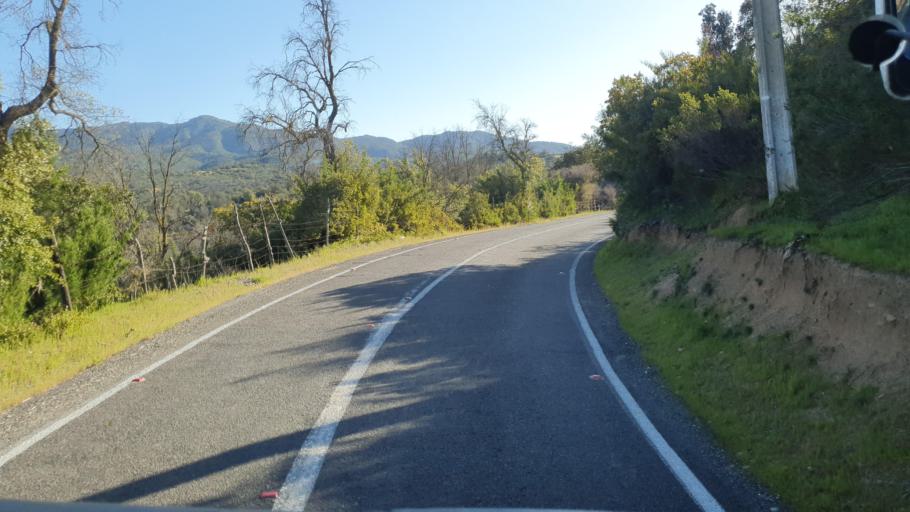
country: CL
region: Valparaiso
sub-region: Provincia de Marga Marga
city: Limache
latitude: -33.1937
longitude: -71.2059
